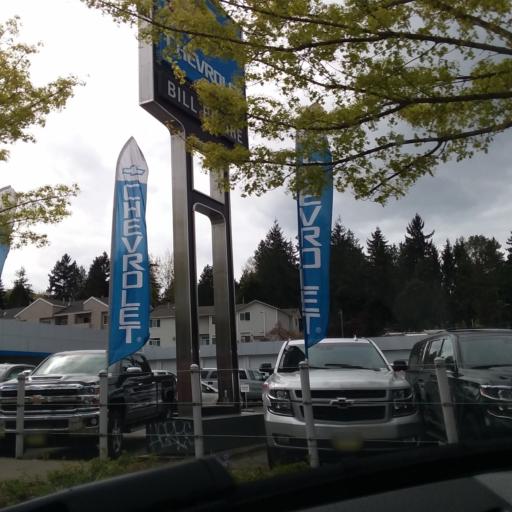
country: US
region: Washington
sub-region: King County
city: Lake Forest Park
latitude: 47.7117
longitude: -122.3000
